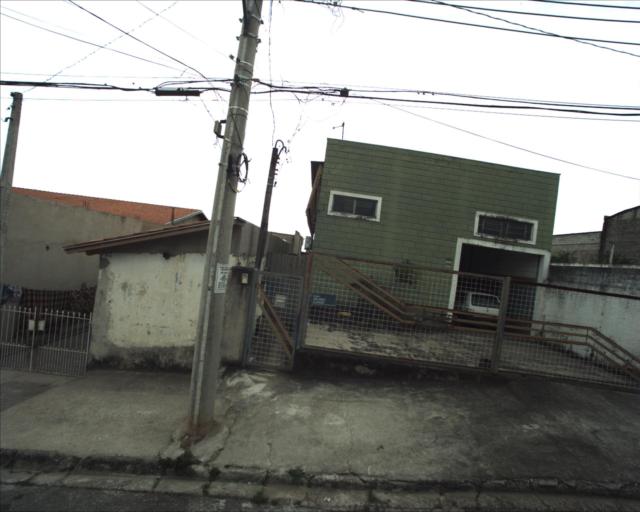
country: BR
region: Sao Paulo
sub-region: Sorocaba
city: Sorocaba
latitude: -23.4621
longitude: -47.4412
